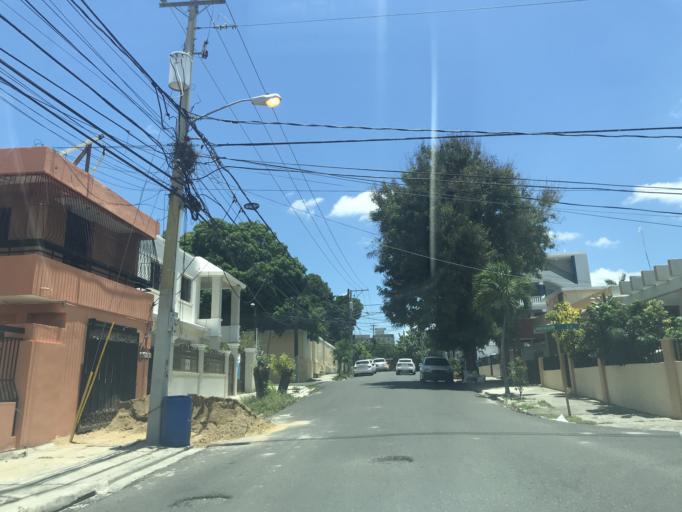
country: DO
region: Santiago
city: Santiago de los Caballeros
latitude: 19.4420
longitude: -70.6980
